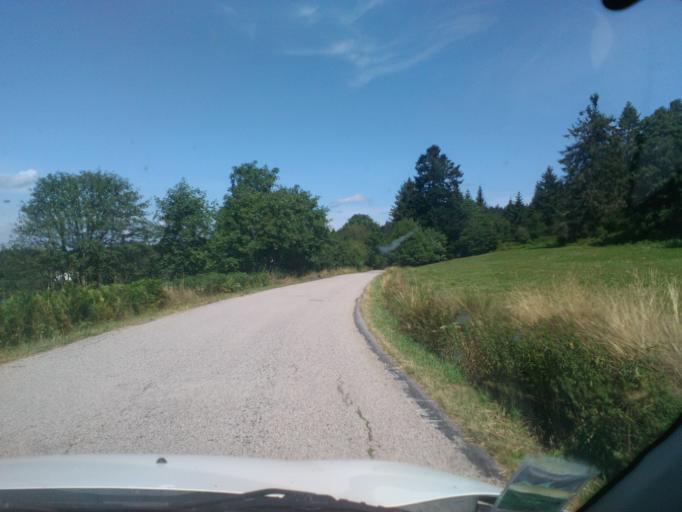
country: FR
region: Lorraine
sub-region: Departement des Vosges
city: Le Tholy
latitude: 48.0428
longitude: 6.7725
